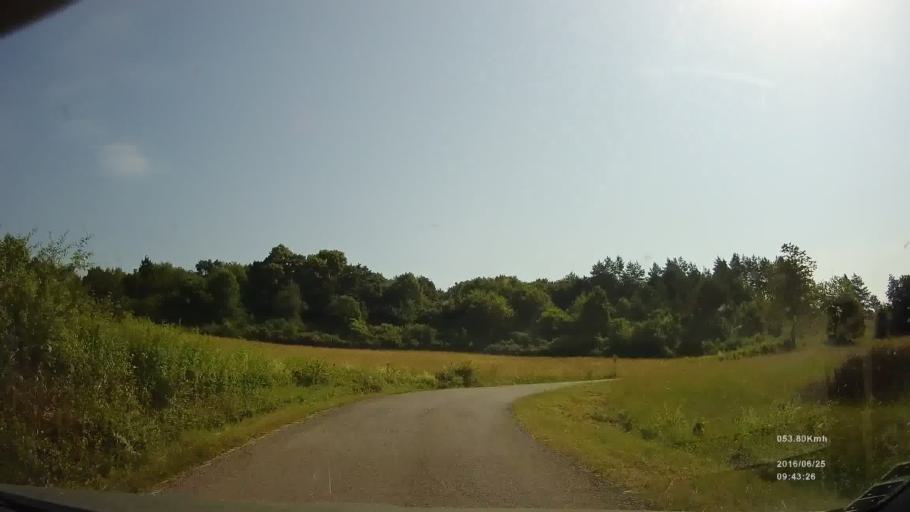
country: SK
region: Banskobystricky
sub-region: Okres Banska Bystrica
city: Banska Bystrica
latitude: 48.7052
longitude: 19.2221
